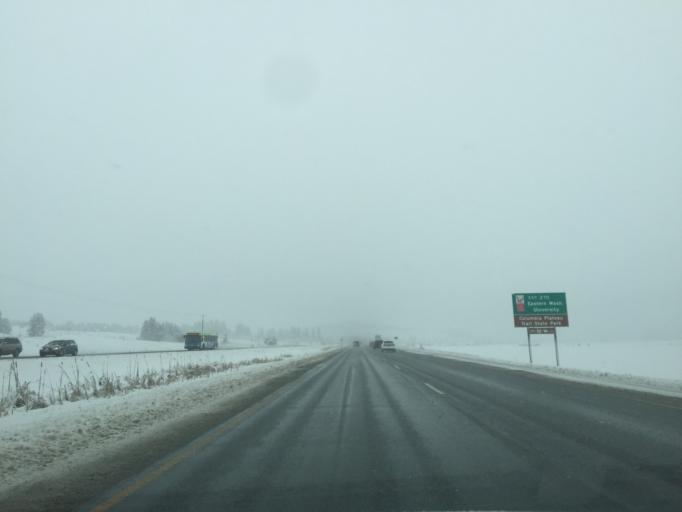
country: US
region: Washington
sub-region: Spokane County
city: Airway Heights
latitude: 47.5748
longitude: -117.5835
